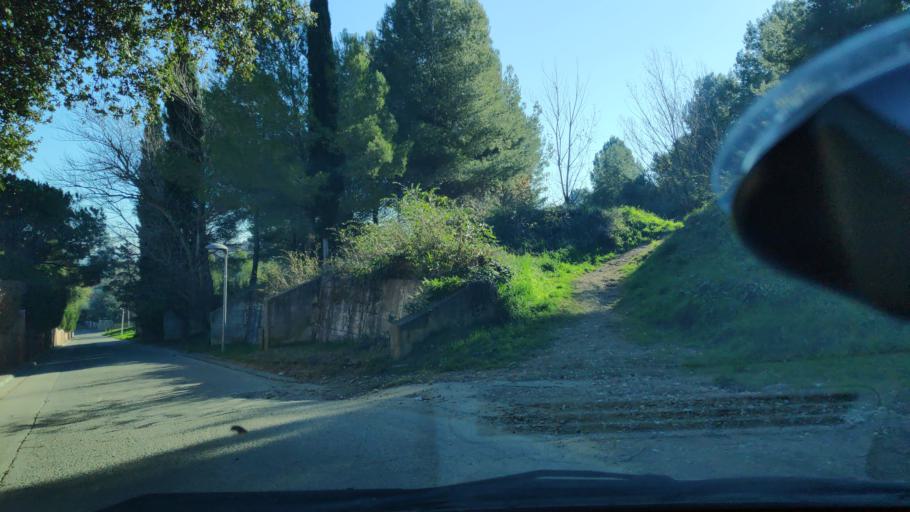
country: ES
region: Catalonia
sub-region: Provincia de Barcelona
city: Sant Quirze del Valles
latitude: 41.5244
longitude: 2.0687
